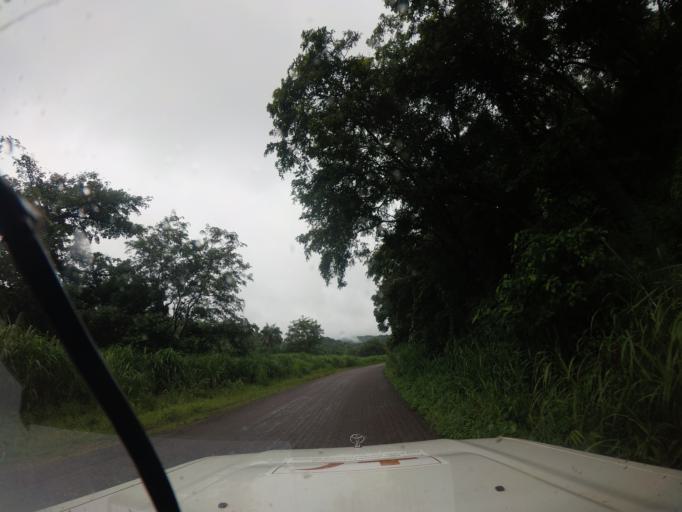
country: SL
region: Northern Province
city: Bumbuna
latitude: 9.3366
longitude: -11.8378
